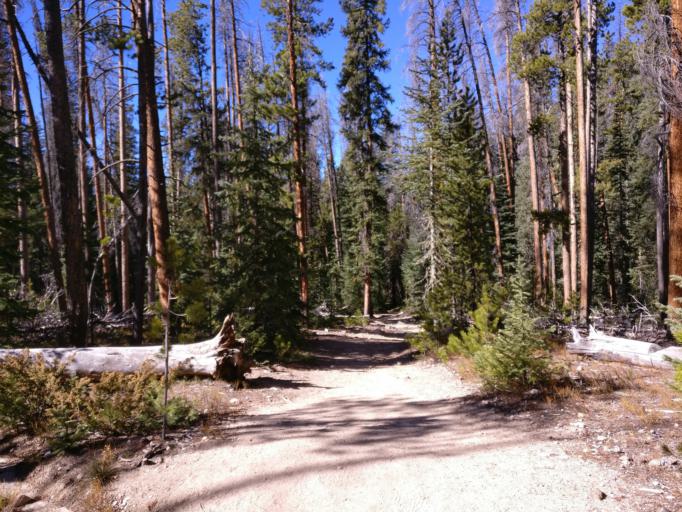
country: US
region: Colorado
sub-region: Grand County
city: Granby
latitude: 40.3107
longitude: -105.8265
